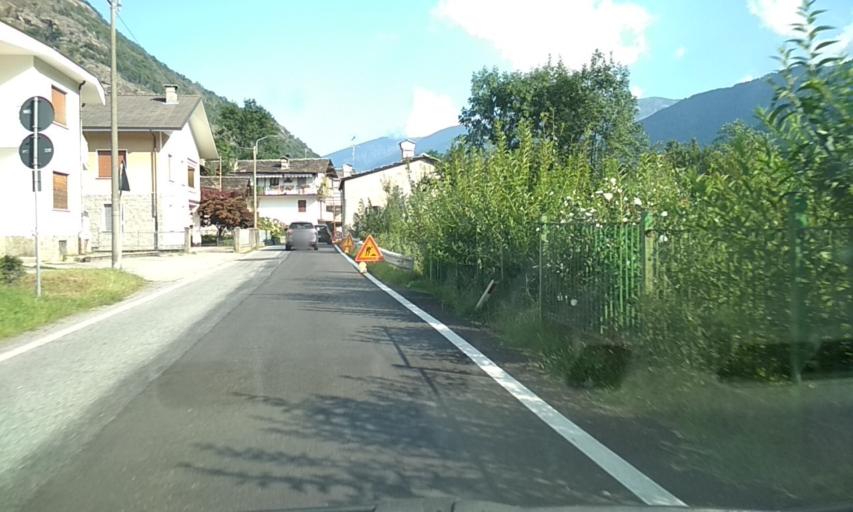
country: IT
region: Piedmont
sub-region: Provincia di Torino
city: Locana
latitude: 45.4322
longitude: 7.4300
